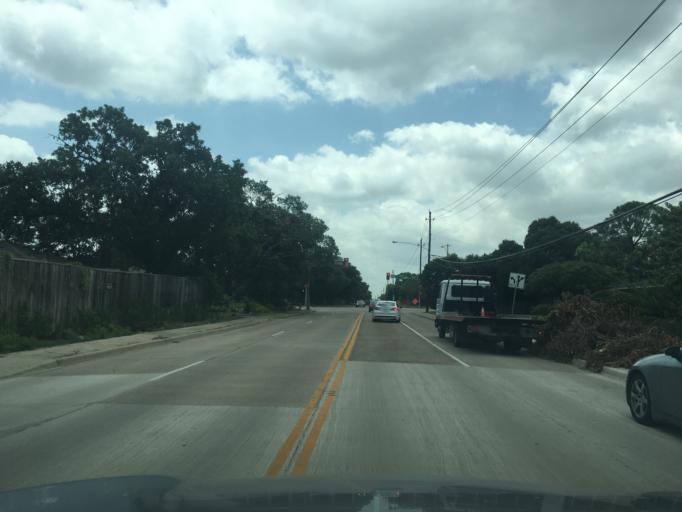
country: US
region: Texas
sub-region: Dallas County
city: Addison
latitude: 32.9104
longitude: -96.8296
